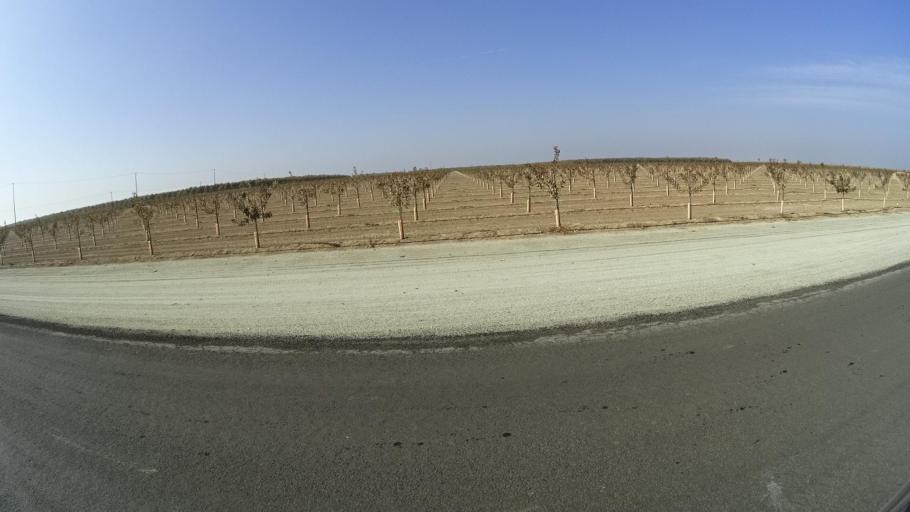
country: US
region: California
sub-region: Kern County
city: McFarland
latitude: 35.6326
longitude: -119.1866
